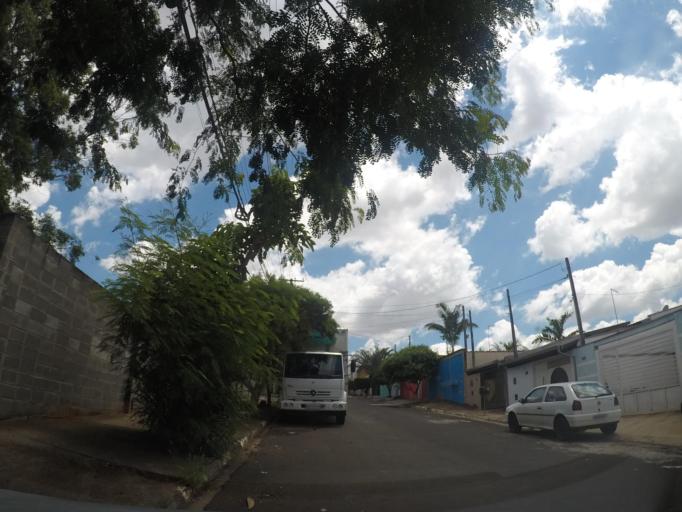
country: BR
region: Sao Paulo
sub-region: Hortolandia
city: Hortolandia
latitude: -22.8199
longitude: -47.2052
